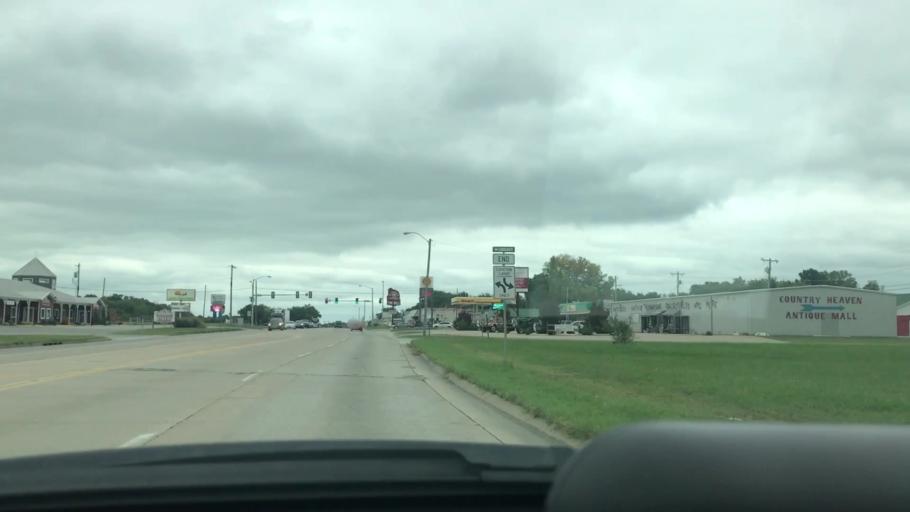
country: US
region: Oklahoma
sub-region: Mayes County
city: Chouteau
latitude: 36.1847
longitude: -95.3428
